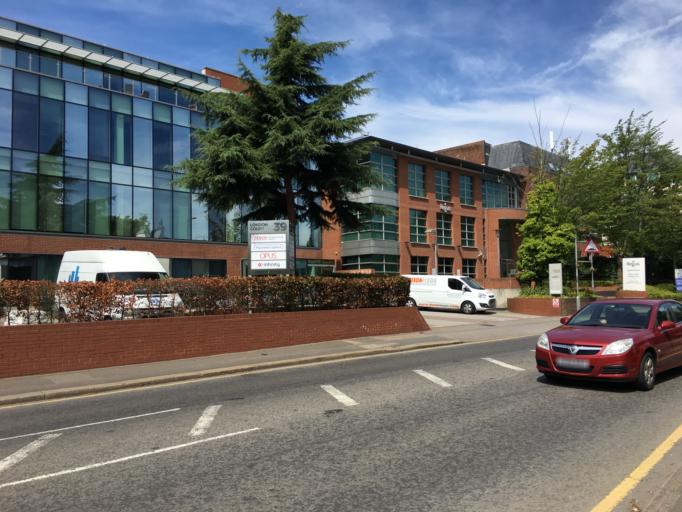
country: GB
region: England
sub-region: Surrey
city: Reigate
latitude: 51.2407
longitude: -0.2054
